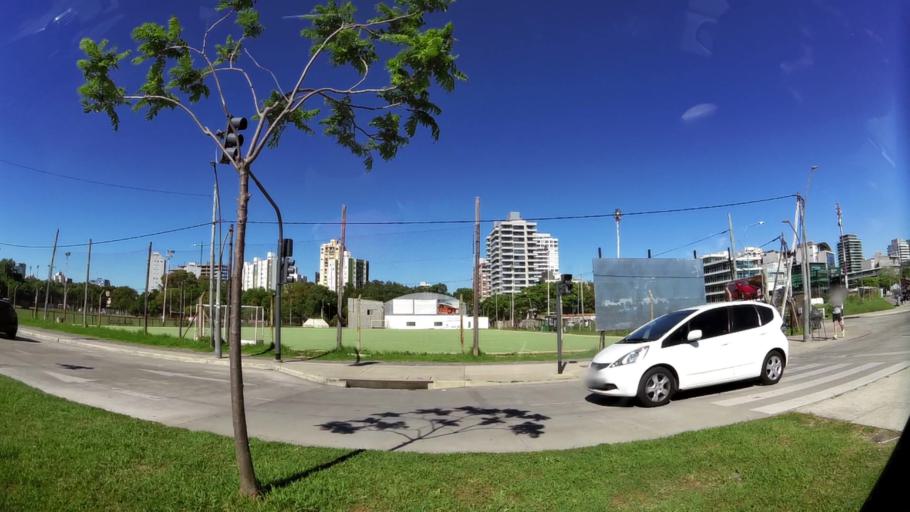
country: AR
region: Buenos Aires
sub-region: Partido de Vicente Lopez
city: Olivos
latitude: -34.5210
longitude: -58.4698
